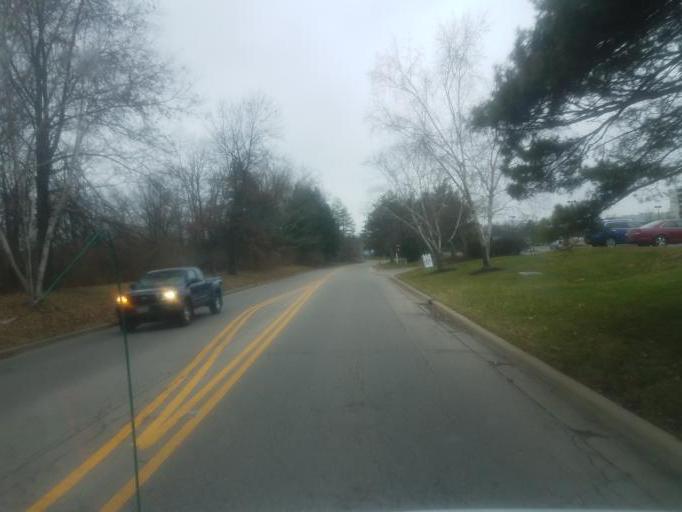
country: US
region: Ohio
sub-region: Franklin County
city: Minerva Park
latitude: 40.1015
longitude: -82.9417
